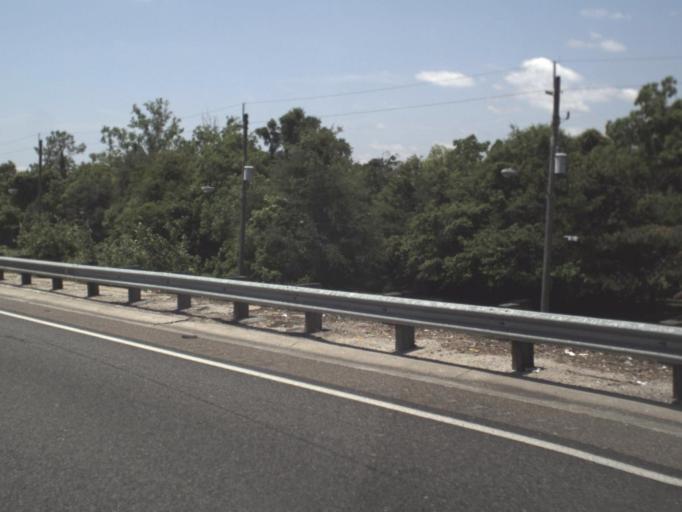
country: US
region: Florida
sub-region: Duval County
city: Jacksonville
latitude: 30.3427
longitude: -81.6683
